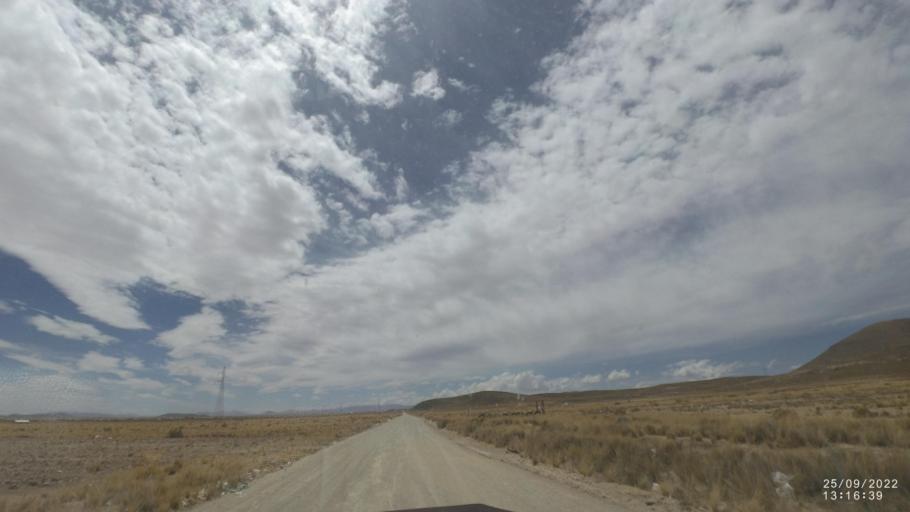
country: BO
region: Oruro
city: Oruro
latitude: -17.9161
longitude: -67.0428
